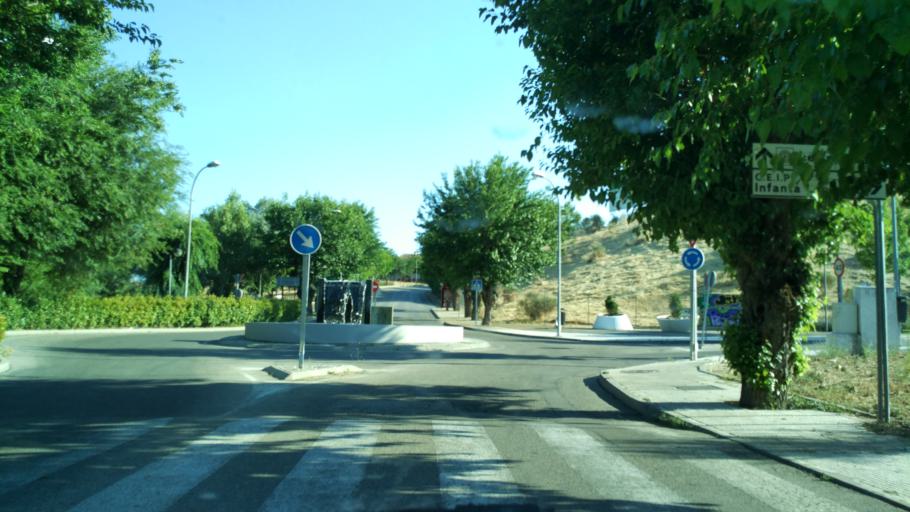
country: ES
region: Madrid
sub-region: Provincia de Madrid
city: San Agustin de Guadalix
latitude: 40.6860
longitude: -3.6109
